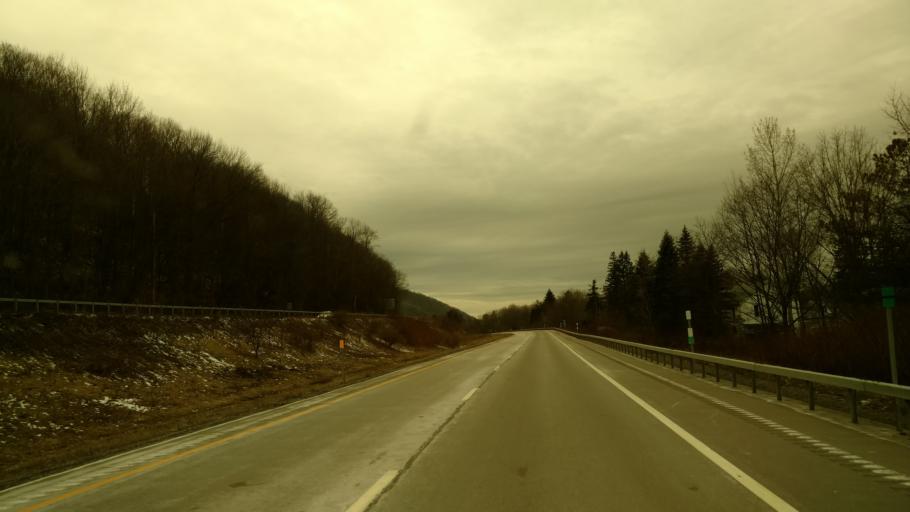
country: US
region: New York
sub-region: Cattaraugus County
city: Salamanca
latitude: 42.1498
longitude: -78.7116
